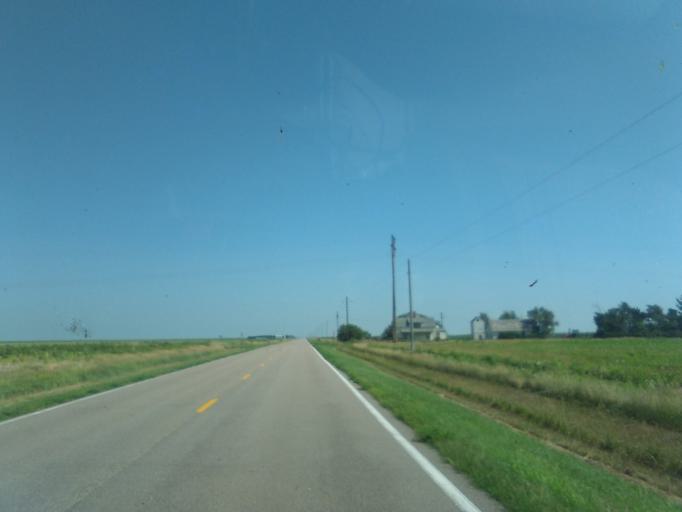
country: US
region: Nebraska
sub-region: Dundy County
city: Benkelman
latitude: 39.8138
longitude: -101.5415
